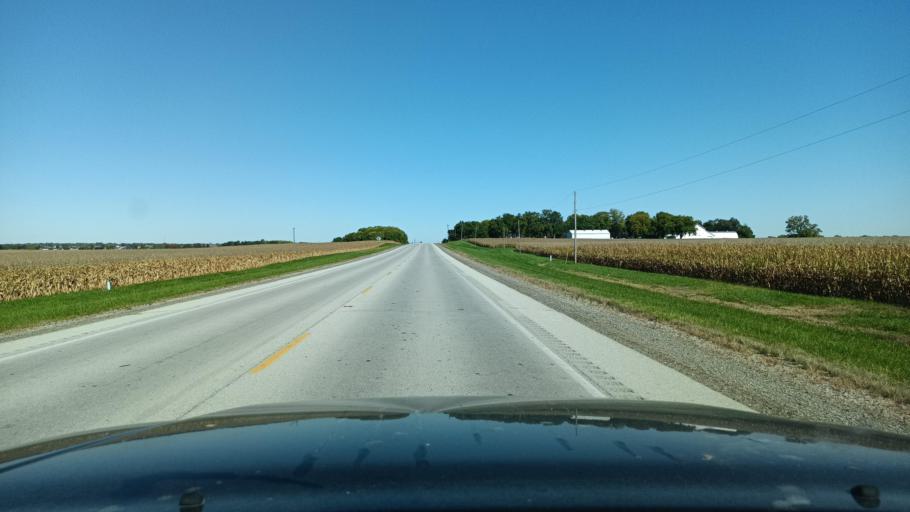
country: US
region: Illinois
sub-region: Champaign County
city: Urbana
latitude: 40.0701
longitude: -88.1619
